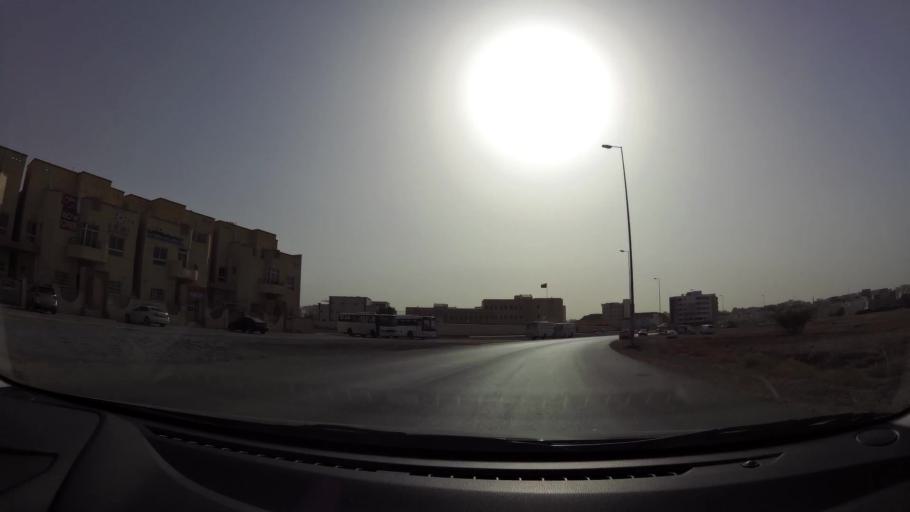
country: OM
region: Muhafazat Masqat
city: Bawshar
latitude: 23.5467
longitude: 58.3657
